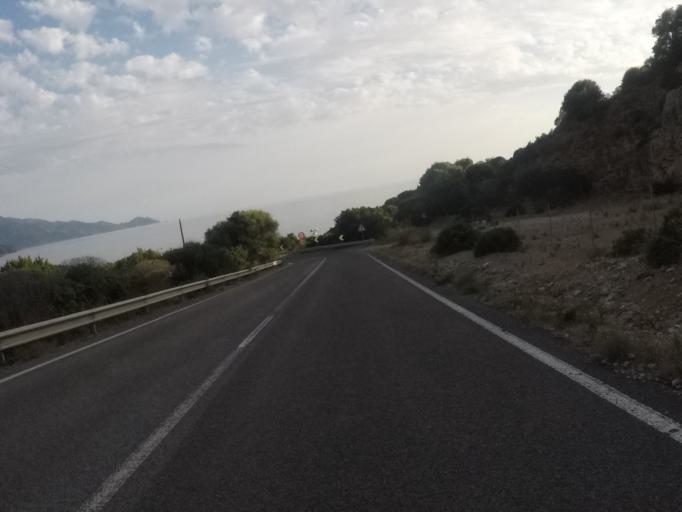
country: IT
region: Sardinia
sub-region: Provincia di Sassari
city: Alghero
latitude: 40.4986
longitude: 8.3681
